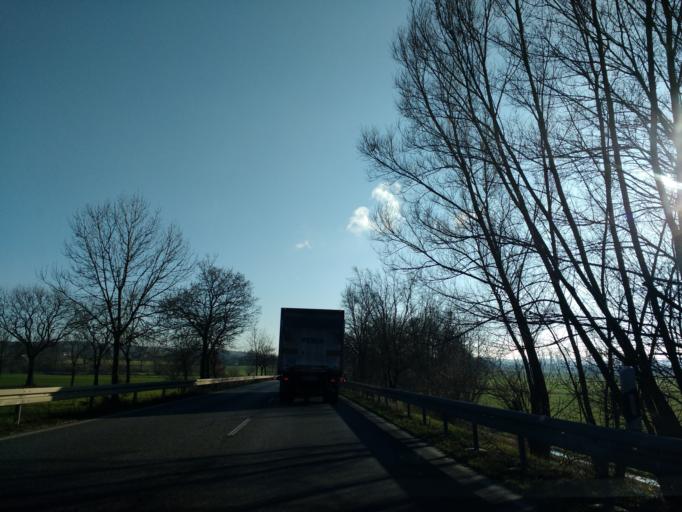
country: DE
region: Hesse
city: Schwalmstadt
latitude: 50.9072
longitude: 9.2581
